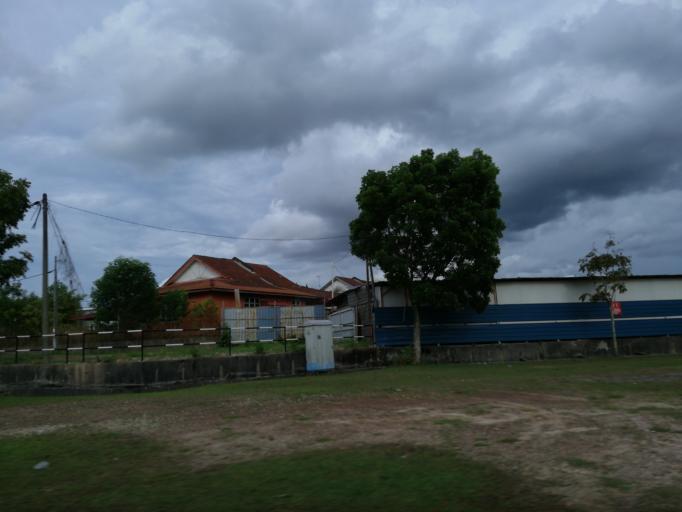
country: MY
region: Penang
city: Tasek Glugor
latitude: 5.4989
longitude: 100.6239
